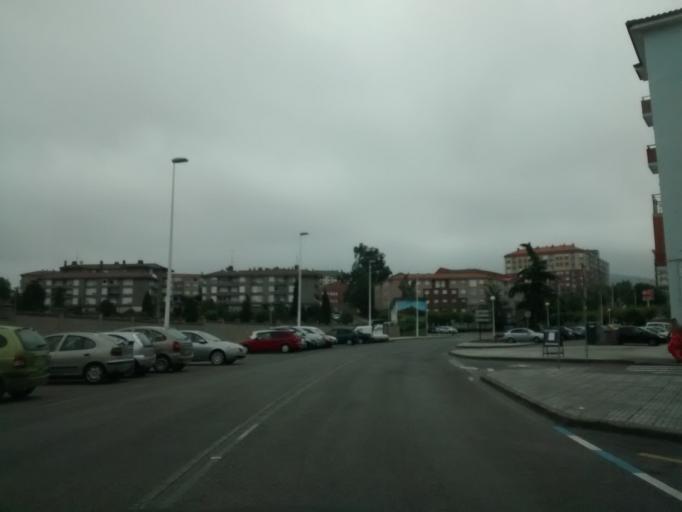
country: ES
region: Cantabria
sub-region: Provincia de Cantabria
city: Torrelavega
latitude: 43.3425
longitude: -4.0508
